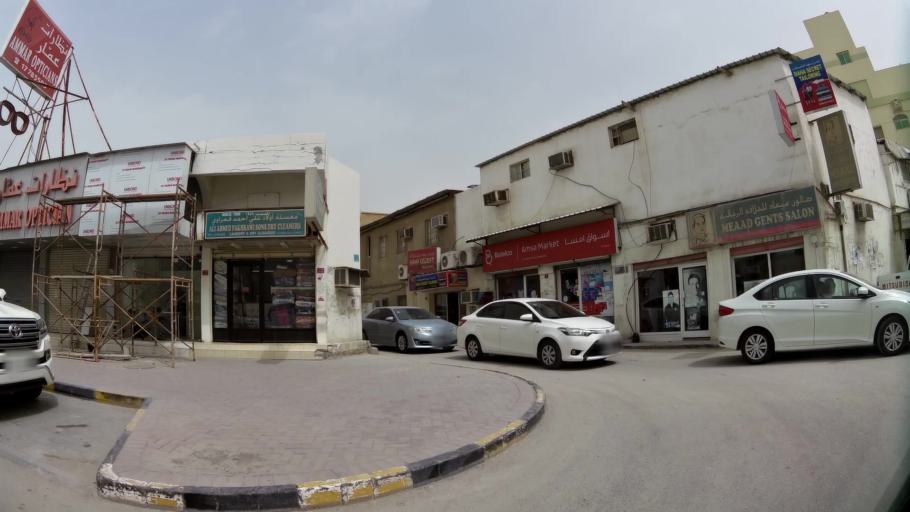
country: BH
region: Northern
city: Madinat `Isa
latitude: 26.1850
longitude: 50.5435
